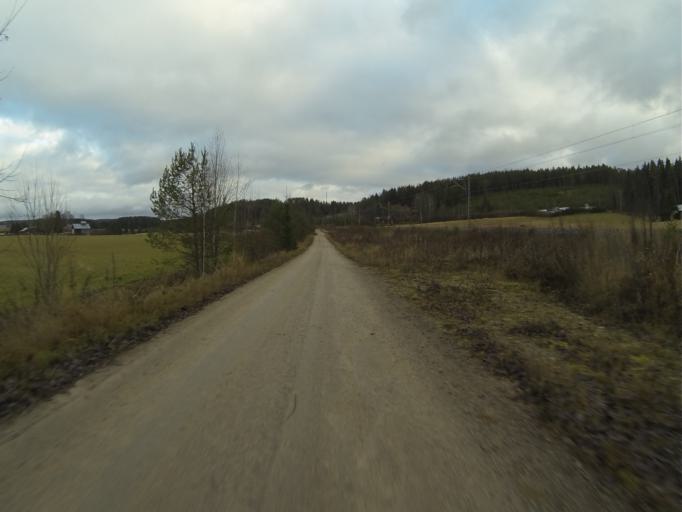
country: FI
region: Varsinais-Suomi
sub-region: Salo
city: Halikko
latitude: 60.4036
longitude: 23.0053
